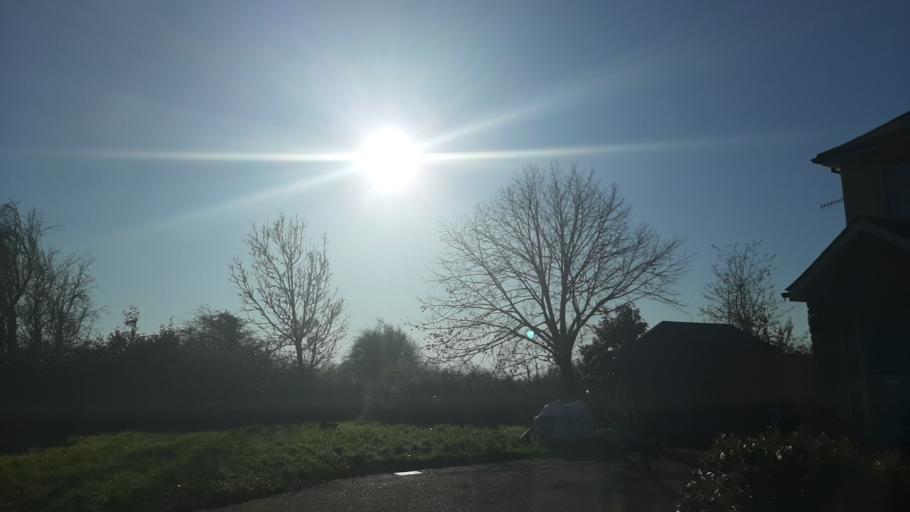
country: IE
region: Leinster
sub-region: Kildare
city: Rathangan
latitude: 53.2178
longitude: -7.0061
